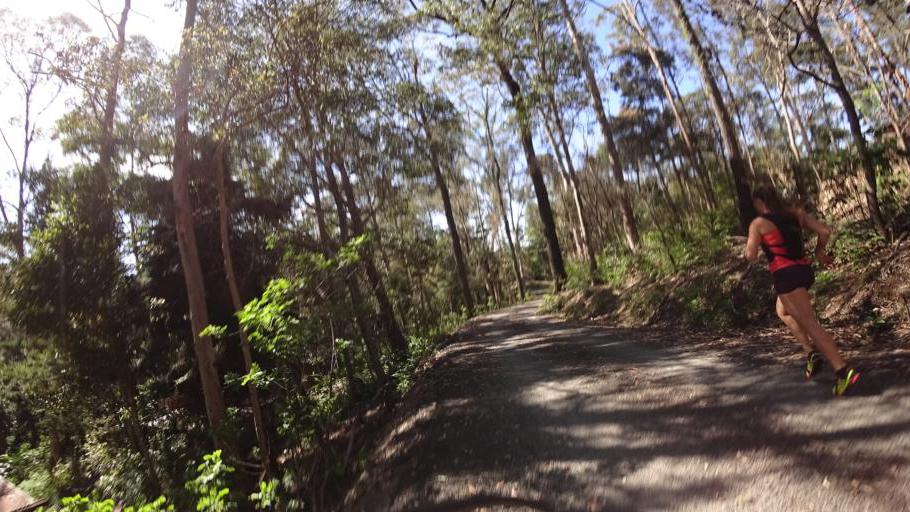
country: AU
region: Queensland
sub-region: Moreton Bay
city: Highvale
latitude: -27.4015
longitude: 152.7832
